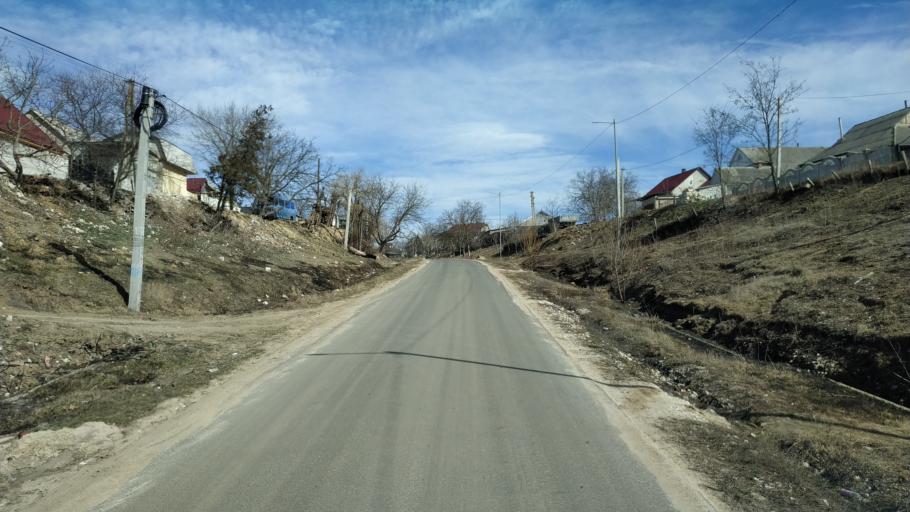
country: MD
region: Nisporeni
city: Nisporeni
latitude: 47.1006
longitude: 28.2948
